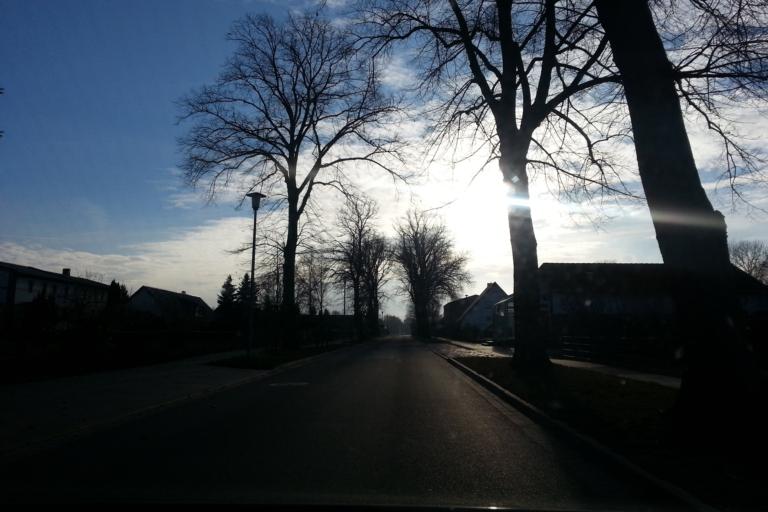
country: DE
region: Mecklenburg-Vorpommern
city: Ferdinandshof
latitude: 53.6428
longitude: 13.8598
